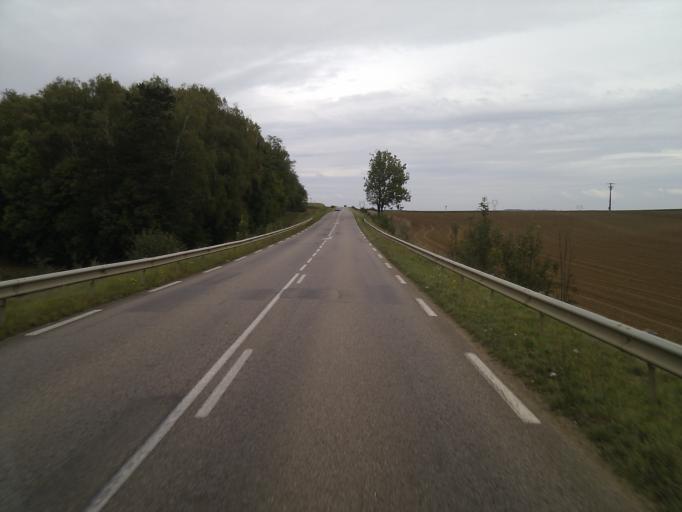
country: FR
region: Lorraine
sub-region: Departement de Meurthe-et-Moselle
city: Colombey-les-Belles
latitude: 48.4635
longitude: 5.8192
